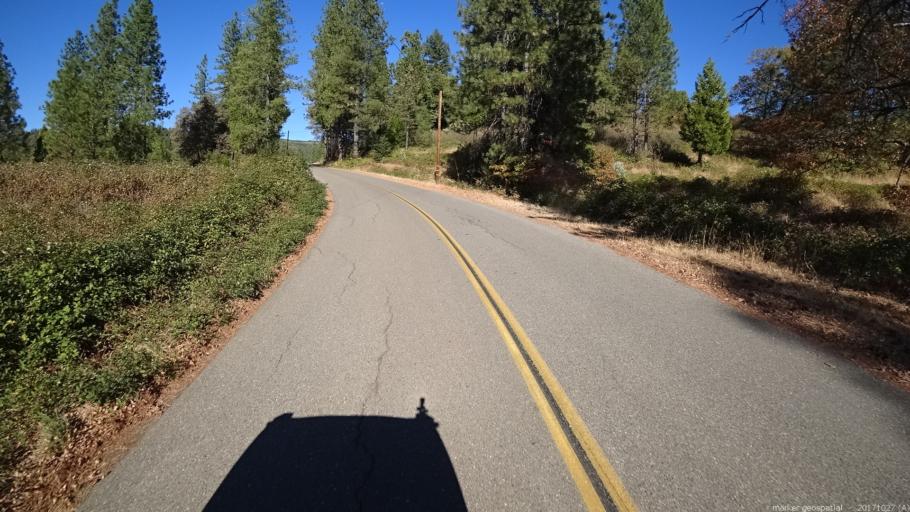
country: US
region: California
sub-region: Shasta County
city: Shingletown
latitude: 40.6730
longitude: -121.8814
